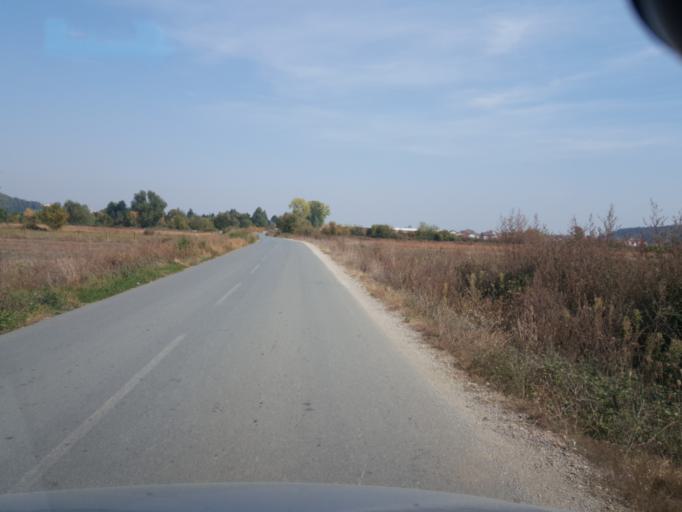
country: XK
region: Gjakova
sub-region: Komuna e Gjakoves
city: Gjakove
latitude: 42.3698
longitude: 20.4021
